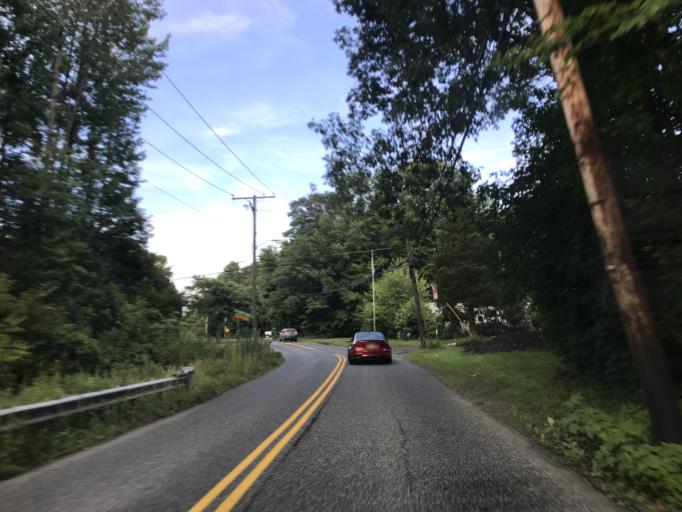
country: US
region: Maryland
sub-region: Harford County
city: Aberdeen
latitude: 39.5156
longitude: -76.1941
